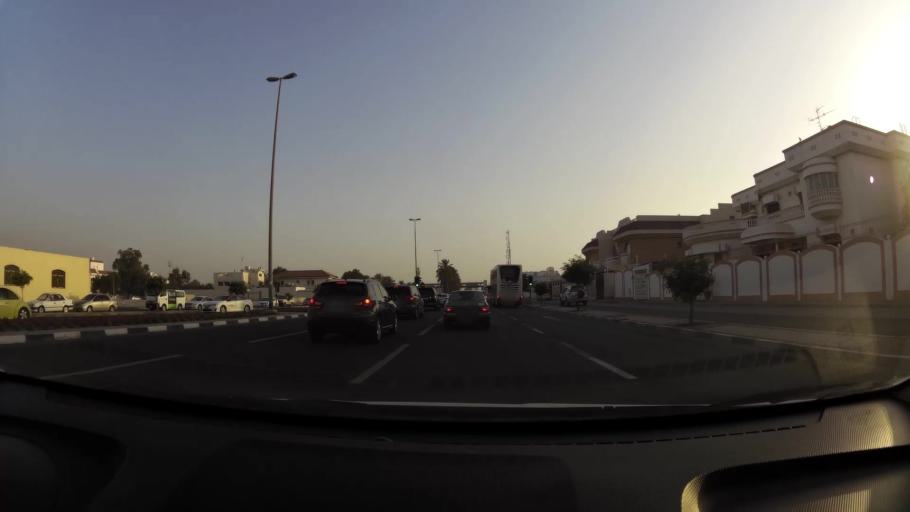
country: AE
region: Ash Shariqah
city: Sharjah
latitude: 25.2872
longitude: 55.3424
